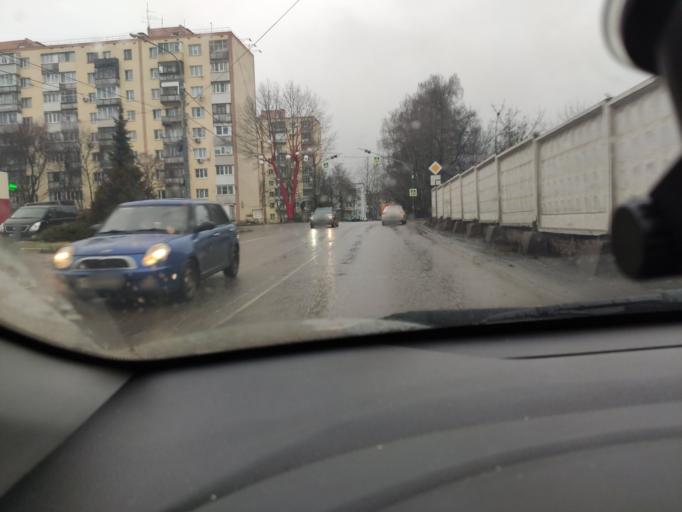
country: RU
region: Moskovskaya
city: Biryulevo Zapadnoye
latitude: 55.5639
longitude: 37.6457
